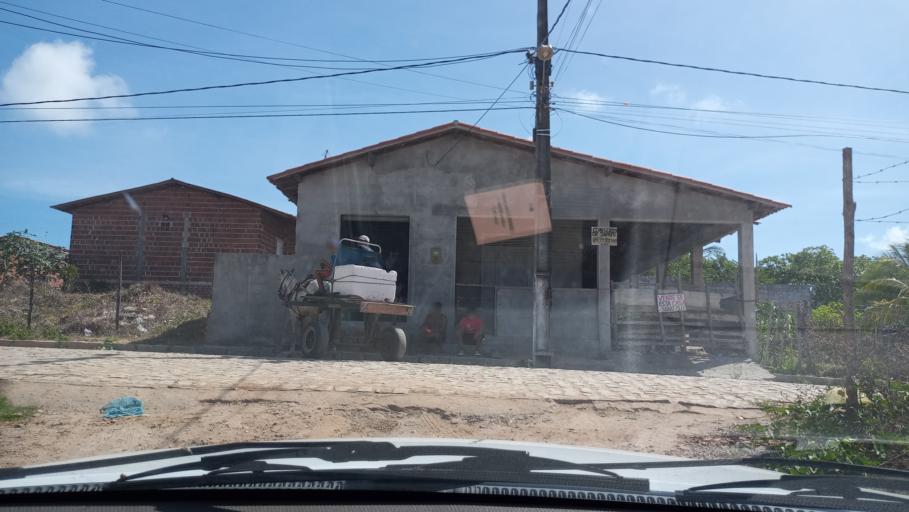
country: BR
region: Rio Grande do Norte
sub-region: Maxaranguape
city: Sao Miguel
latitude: -5.5159
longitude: -35.2630
